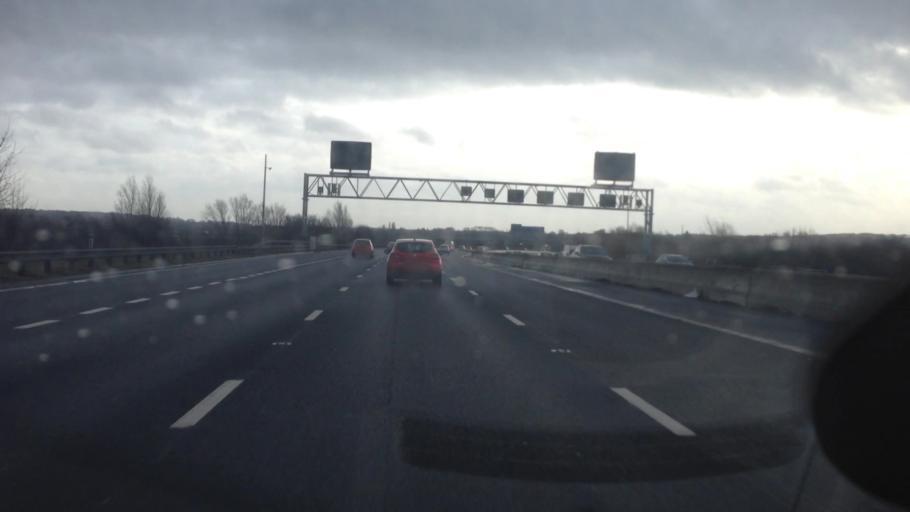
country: GB
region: England
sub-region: City and Borough of Wakefield
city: Crigglestone
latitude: 53.6590
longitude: -1.5311
